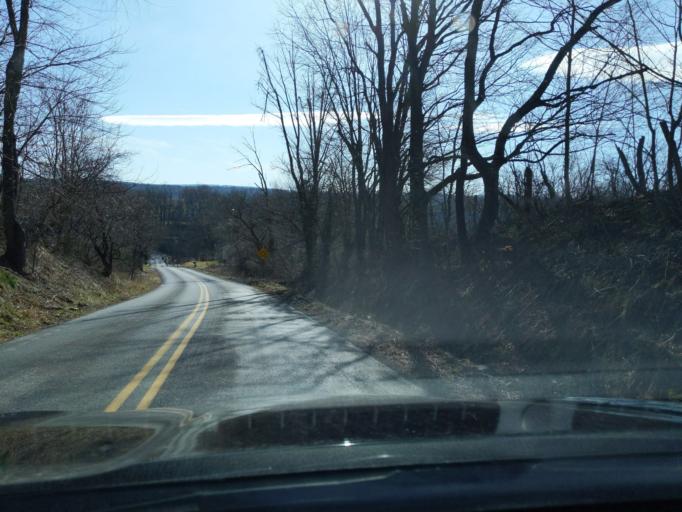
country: US
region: Pennsylvania
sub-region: Blair County
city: Williamsburg
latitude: 40.4223
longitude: -78.2760
